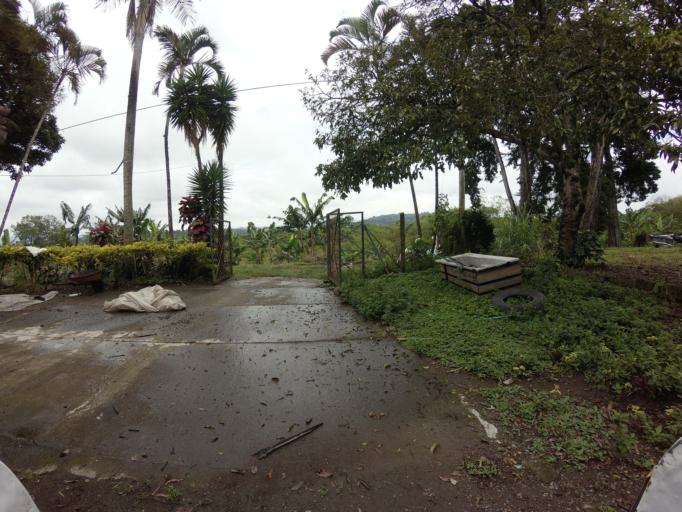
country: CO
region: Valle del Cauca
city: Ulloa
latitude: 4.6997
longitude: -75.7314
